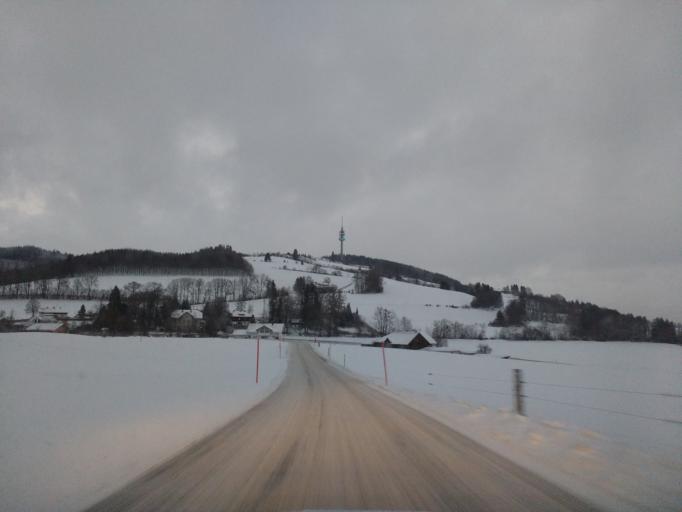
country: DE
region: Bavaria
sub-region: Swabia
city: Buchenberg
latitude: 47.7166
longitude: 10.2170
